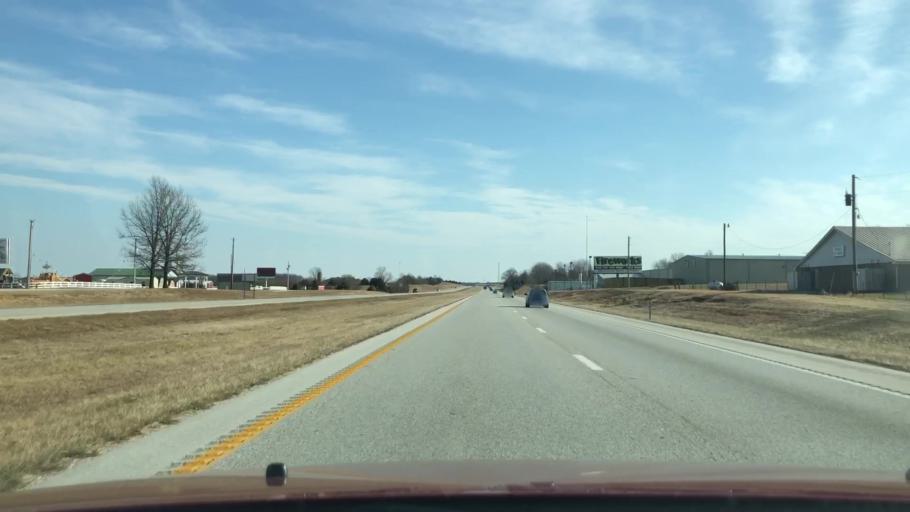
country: US
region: Missouri
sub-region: Webster County
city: Seymour
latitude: 37.1565
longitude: -92.7830
